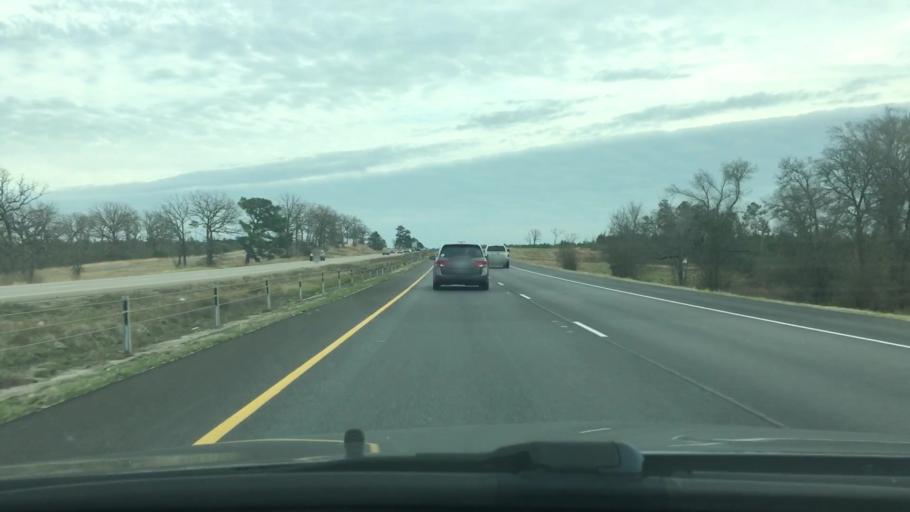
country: US
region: Texas
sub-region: Madison County
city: Madisonville
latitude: 30.8479
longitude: -95.7338
